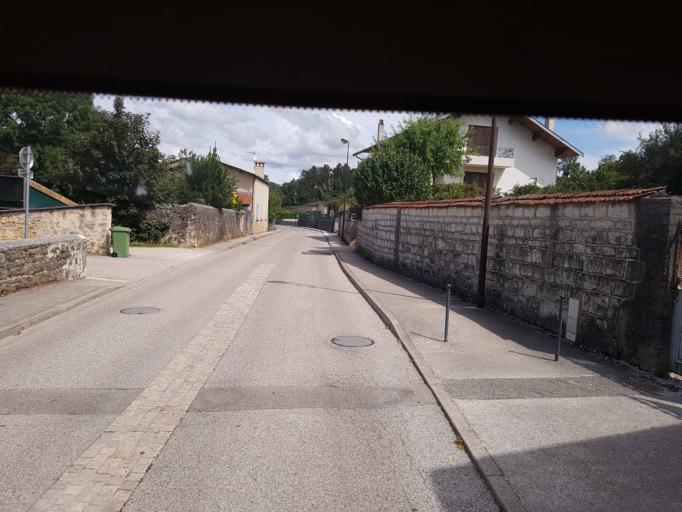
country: FR
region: Rhone-Alpes
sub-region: Departement de l'Ain
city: Poncin
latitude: 46.0867
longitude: 5.4066
